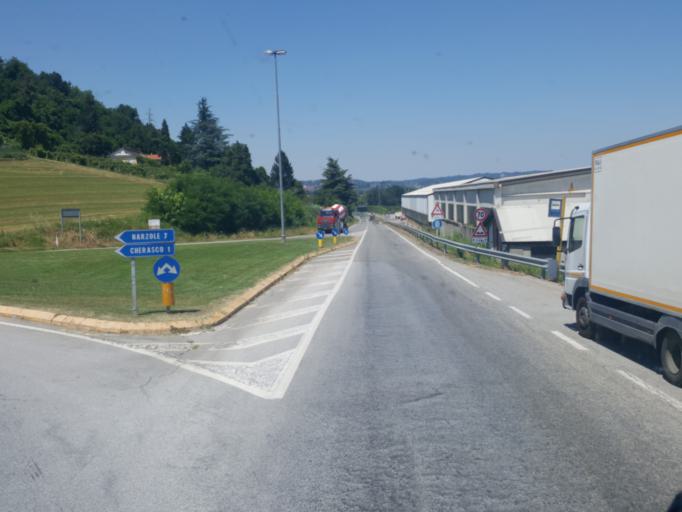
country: IT
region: Piedmont
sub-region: Provincia di Cuneo
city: Cherasco
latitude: 44.6510
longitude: 7.8661
